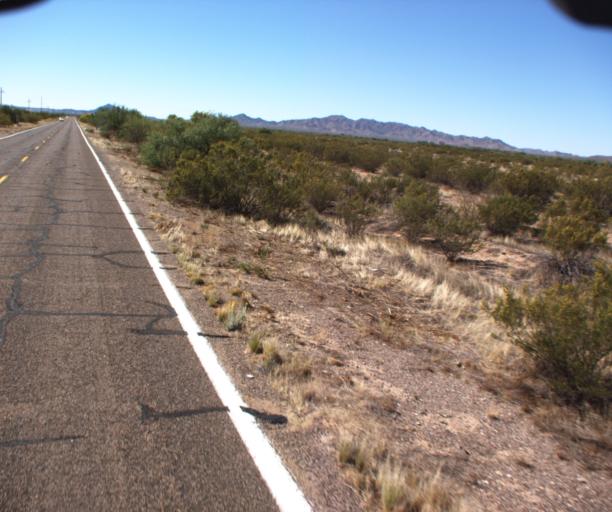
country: US
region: Arizona
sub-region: Pima County
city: Ajo
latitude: 32.4712
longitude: -112.8762
